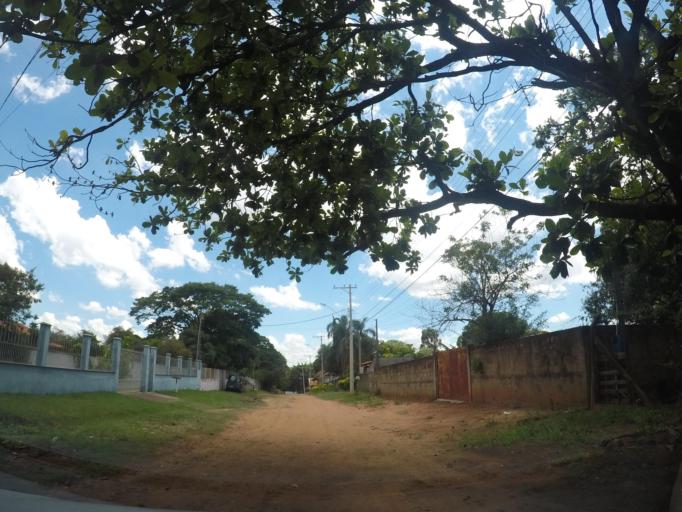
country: BR
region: Sao Paulo
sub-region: Hortolandia
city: Hortolandia
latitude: -22.8434
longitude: -47.2388
